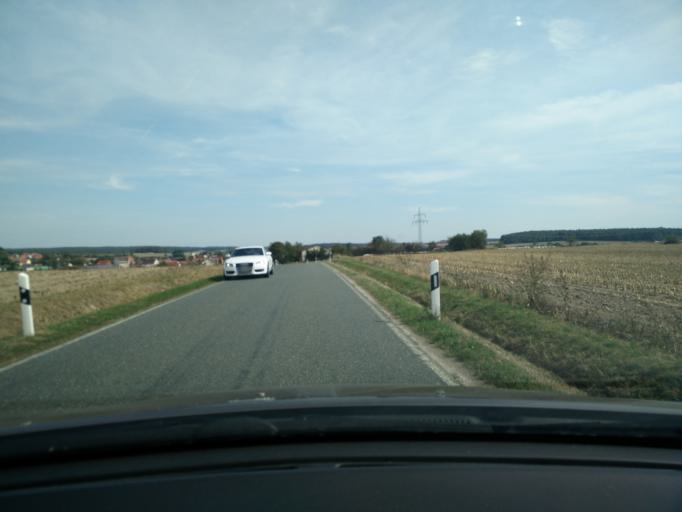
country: DE
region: Bavaria
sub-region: Regierungsbezirk Mittelfranken
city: Emskirchen
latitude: 49.5706
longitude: 10.6979
